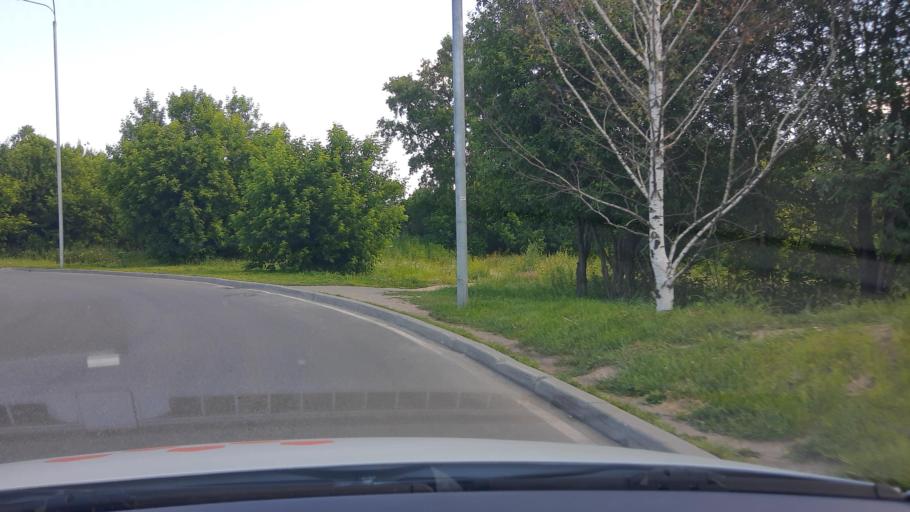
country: RU
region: Moskovskaya
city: Balashikha
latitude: 55.7935
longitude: 37.9487
